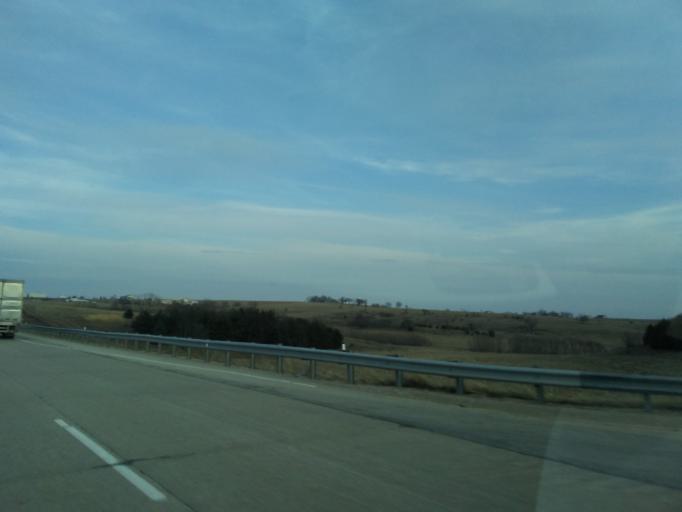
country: US
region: Wisconsin
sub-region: Iowa County
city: Barneveld
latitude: 43.0100
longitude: -89.8434
